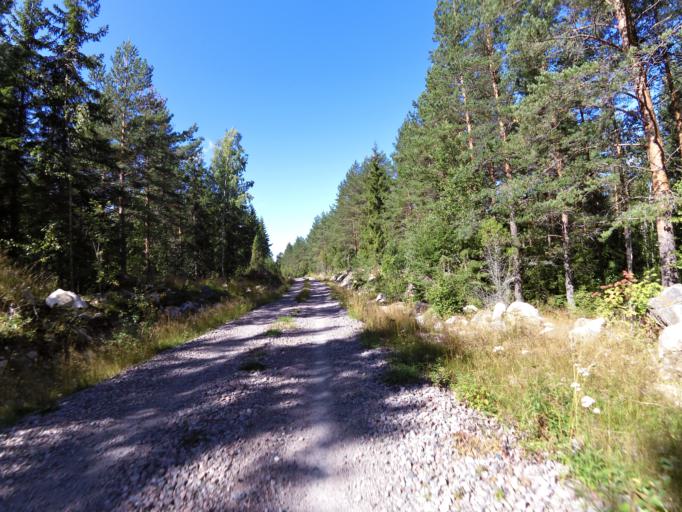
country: SE
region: Gaevleborg
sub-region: Gavle Kommun
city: Valbo
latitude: 60.7297
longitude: 16.9949
